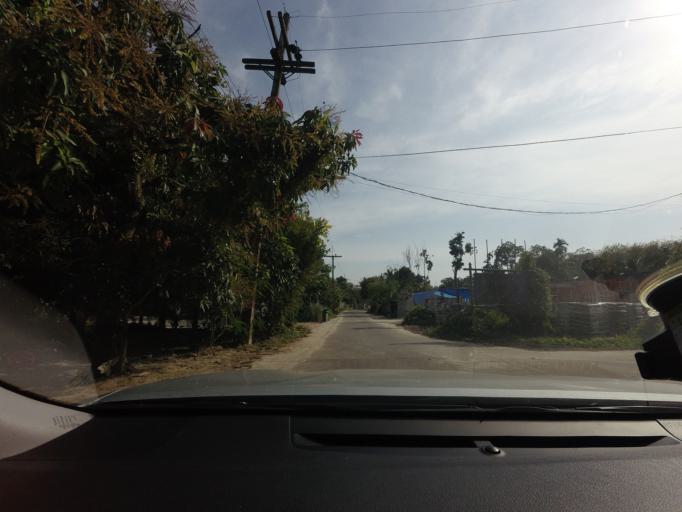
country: TH
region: Narathiwat
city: Ra-ngae
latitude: 6.3109
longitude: 101.7786
